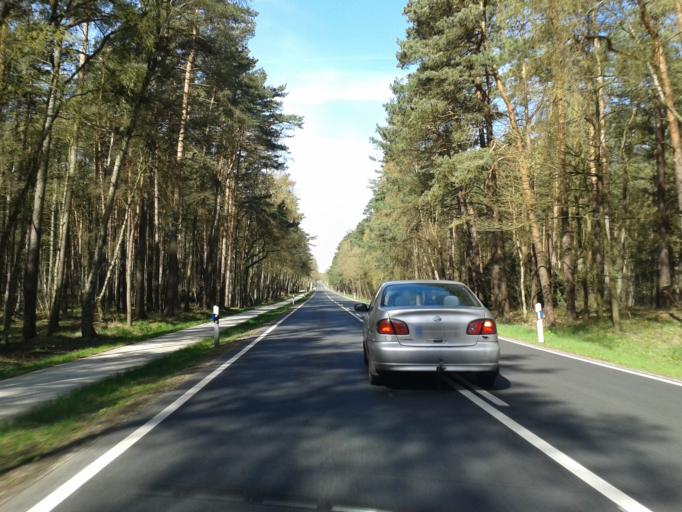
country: DE
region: Lower Saxony
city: Schnega
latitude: 52.9266
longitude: 10.8418
